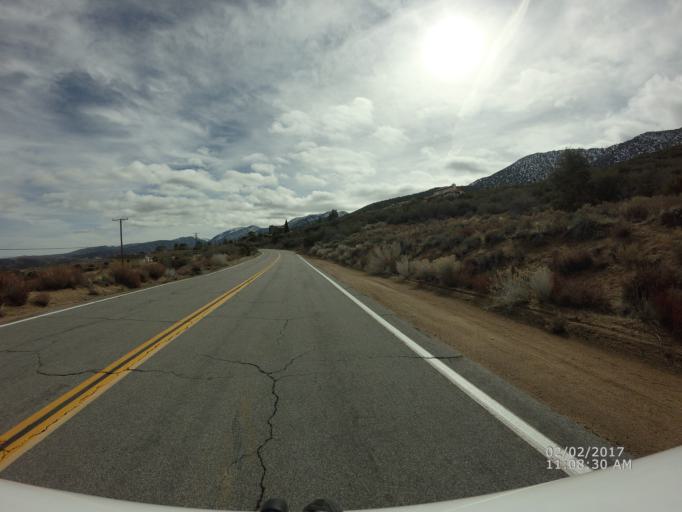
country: US
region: California
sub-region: Los Angeles County
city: Littlerock
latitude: 34.4331
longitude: -117.9263
